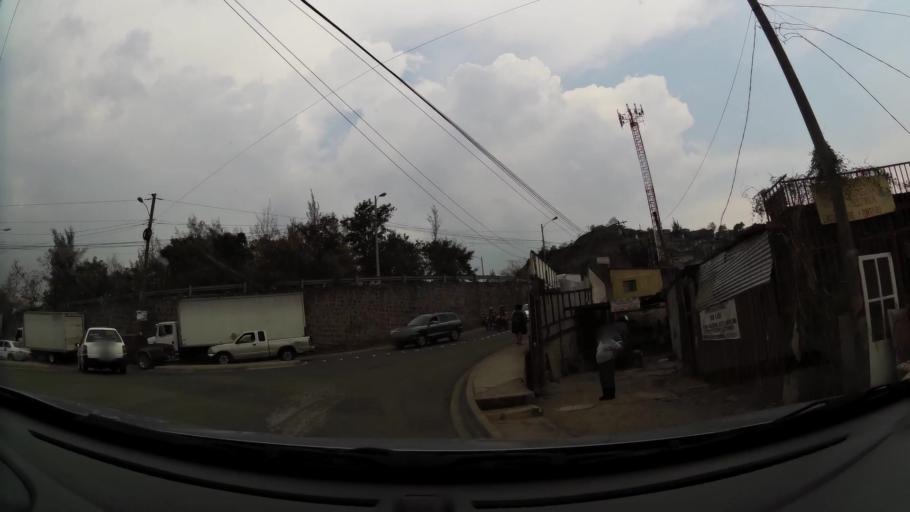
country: HN
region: Francisco Morazan
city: El Tablon
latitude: 14.0649
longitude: -87.1728
